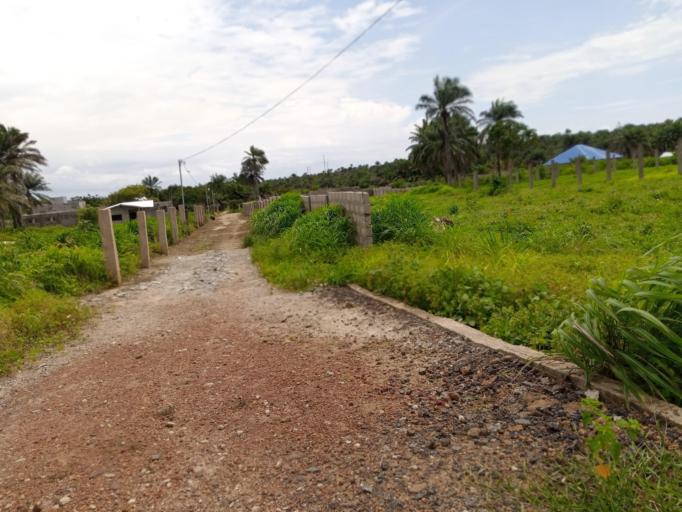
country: SL
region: Northern Province
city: Masoyila
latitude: 8.5506
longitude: -13.1600
